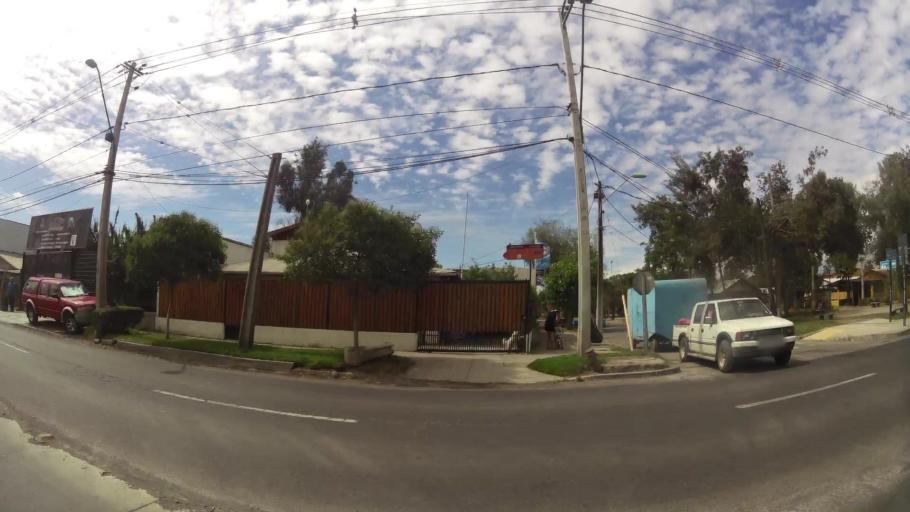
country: CL
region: Santiago Metropolitan
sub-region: Provincia de Santiago
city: La Pintana
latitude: -33.5861
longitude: -70.6567
